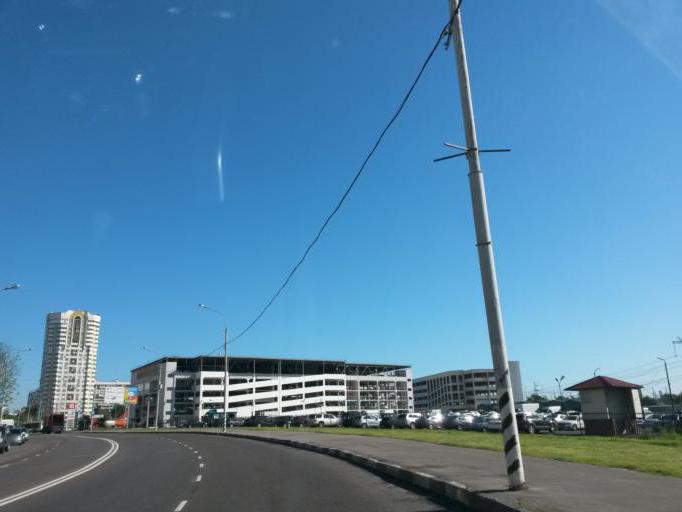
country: RU
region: Moscow
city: Brateyevo
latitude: 55.6327
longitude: 37.7711
